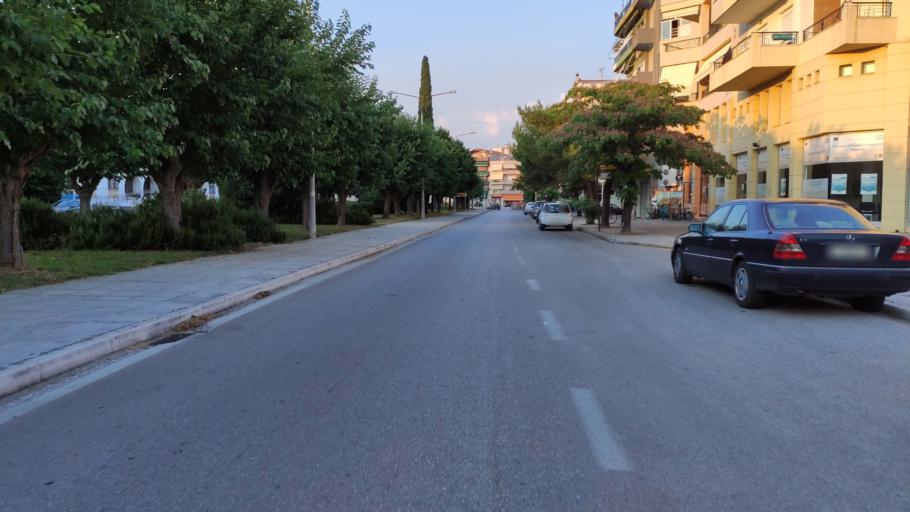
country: GR
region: East Macedonia and Thrace
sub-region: Nomos Rodopis
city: Komotini
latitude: 41.1166
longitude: 25.3956
